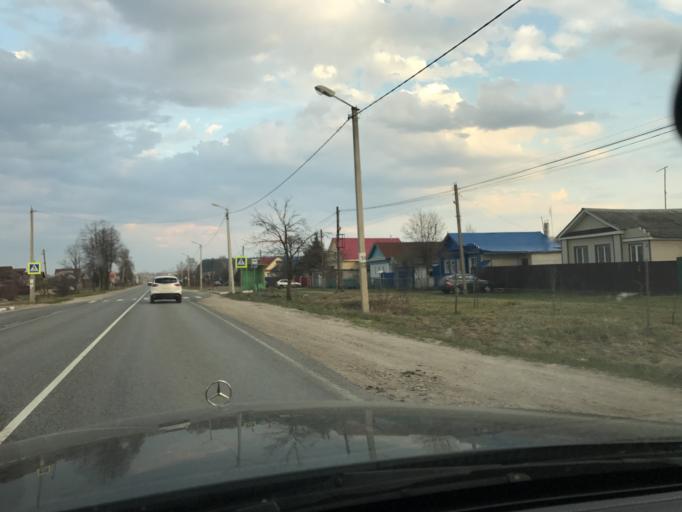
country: RU
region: Vladimir
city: Murom
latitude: 55.6060
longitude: 41.9619
